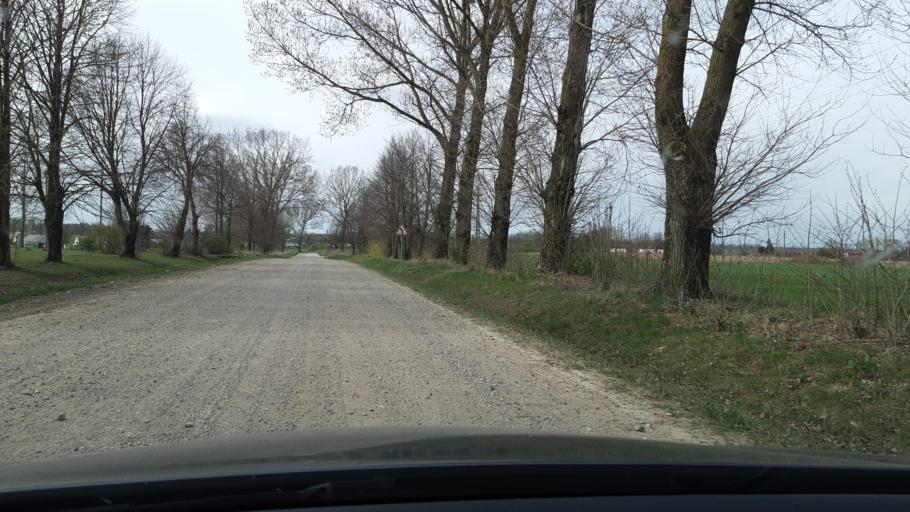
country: LT
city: Virbalis
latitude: 54.6200
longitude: 22.8386
